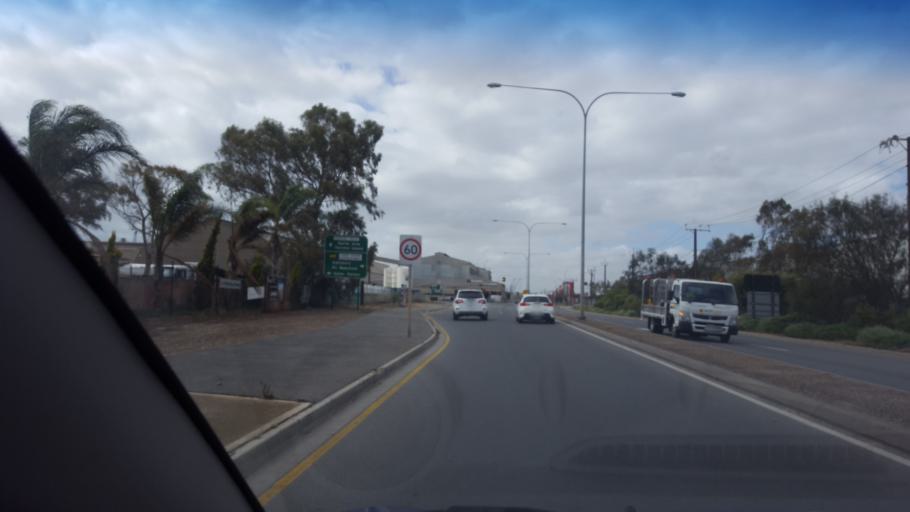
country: AU
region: South Australia
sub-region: Port Adelaide Enfield
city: Alberton
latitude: -34.8429
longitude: 138.5149
